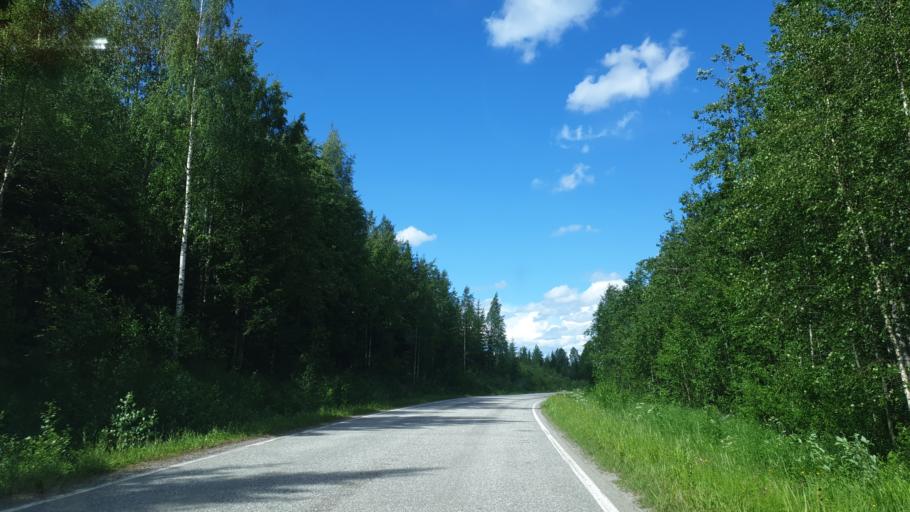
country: FI
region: Northern Savo
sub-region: Koillis-Savo
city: Kaavi
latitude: 63.0299
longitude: 28.6106
